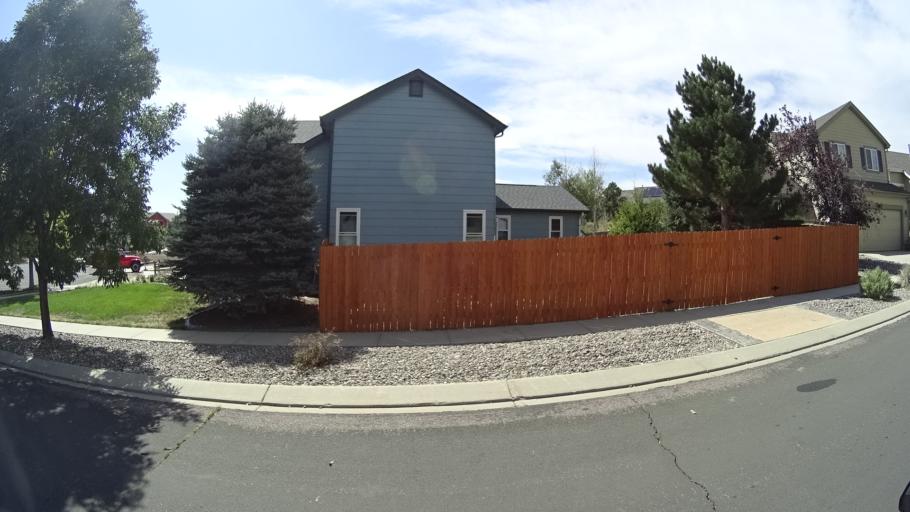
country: US
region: Colorado
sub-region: El Paso County
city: Cimarron Hills
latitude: 38.8984
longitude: -104.7153
